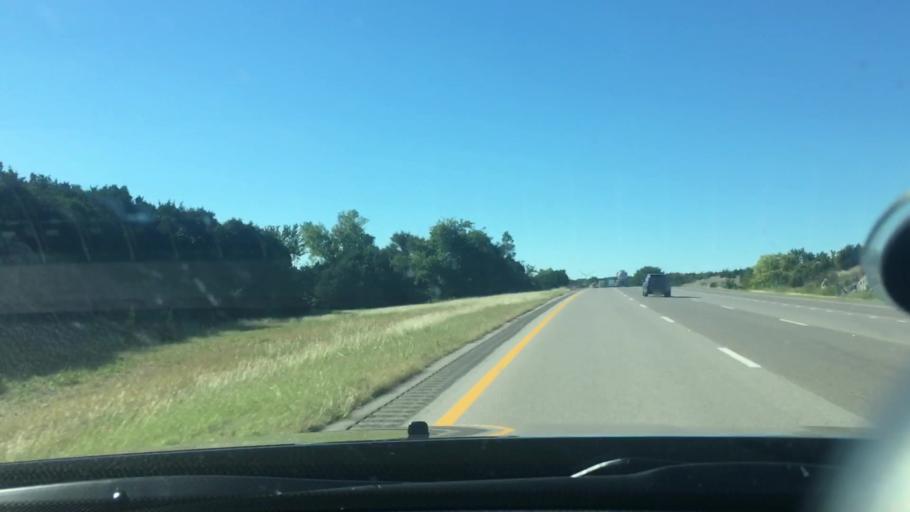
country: US
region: Oklahoma
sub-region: Murray County
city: Davis
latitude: 34.4221
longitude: -97.1354
